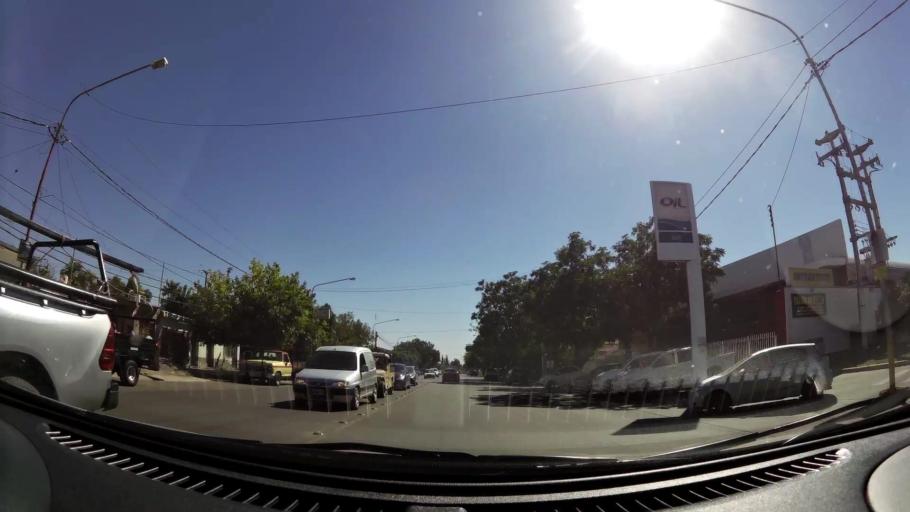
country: AR
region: Mendoza
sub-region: Departamento de Maipu
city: Maipu
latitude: -32.9498
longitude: -68.7872
